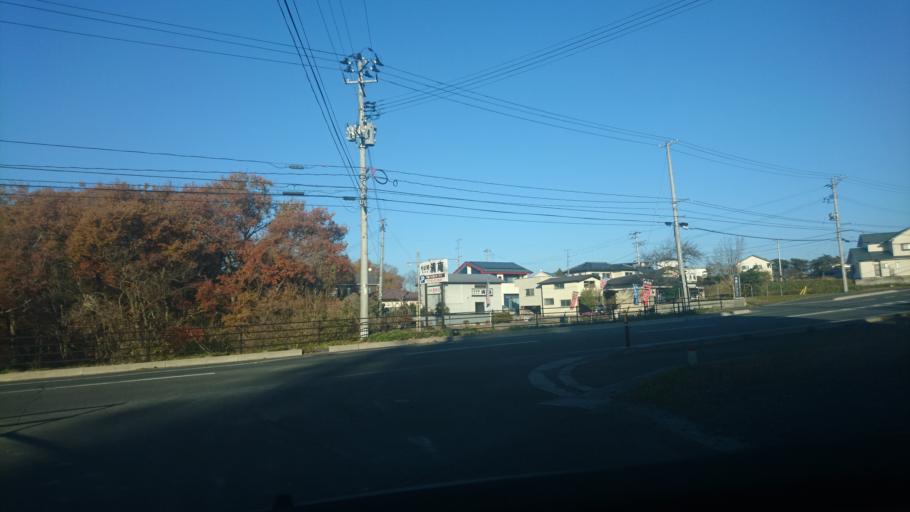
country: JP
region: Iwate
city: Ichinoseki
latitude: 38.9084
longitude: 141.1646
